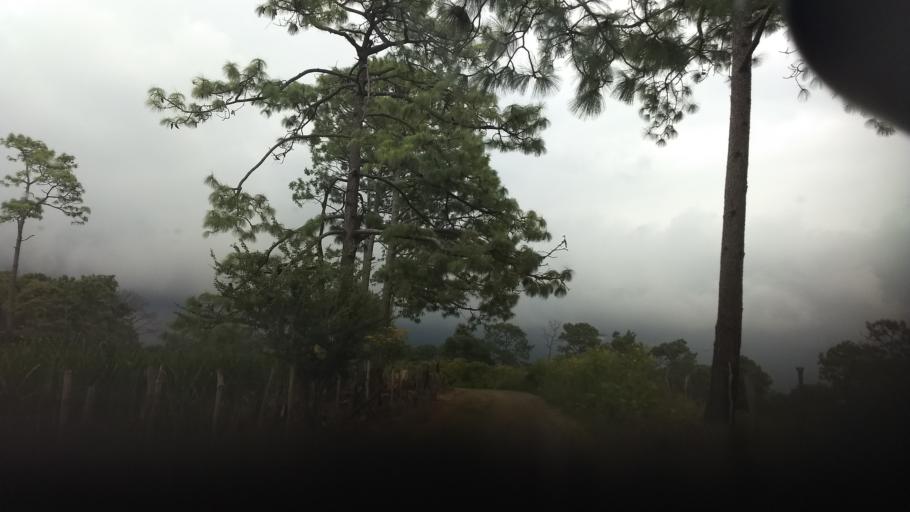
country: MX
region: Colima
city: Cofradia
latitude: 19.4684
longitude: -103.5373
